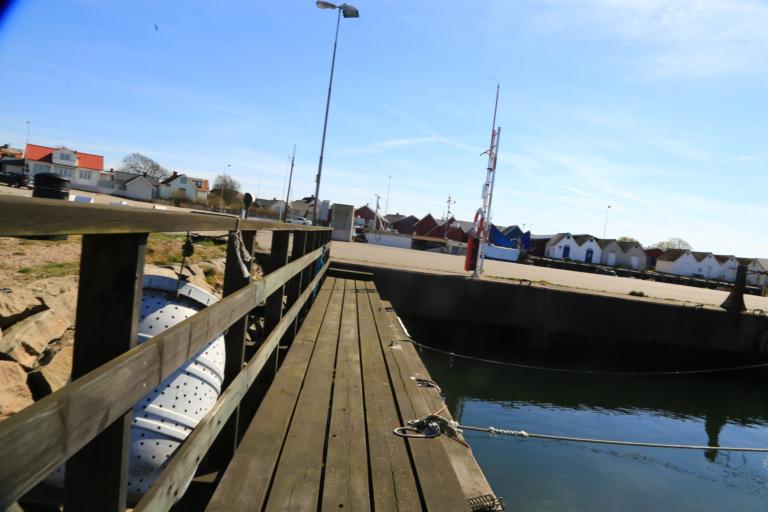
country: SE
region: Halland
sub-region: Varbergs Kommun
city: Traslovslage
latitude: 57.0595
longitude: 12.2745
